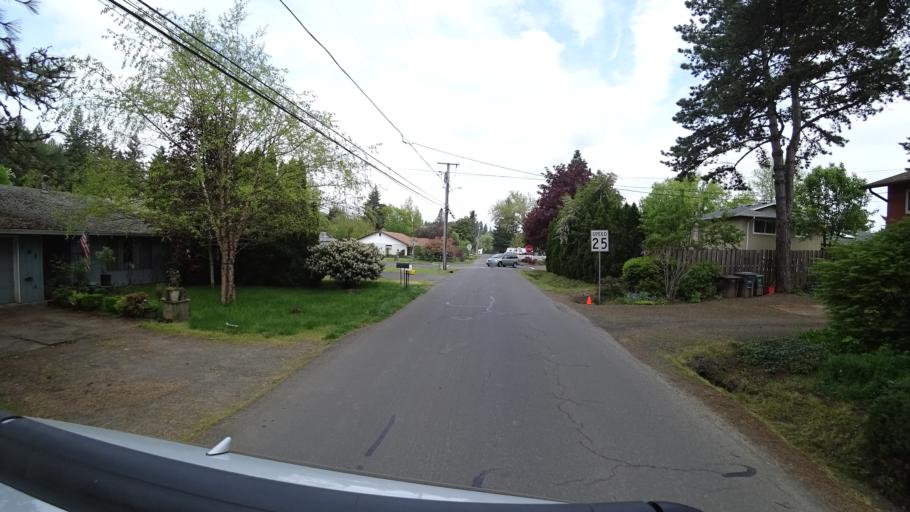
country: US
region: Oregon
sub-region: Washington County
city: Hillsboro
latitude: 45.5298
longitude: -123.0006
